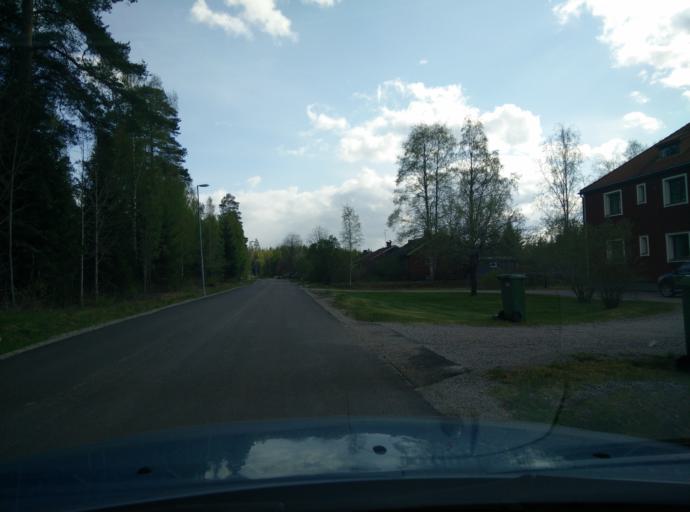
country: SE
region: Vaermland
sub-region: Hagfors Kommun
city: Hagfors
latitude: 60.0215
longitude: 13.6776
